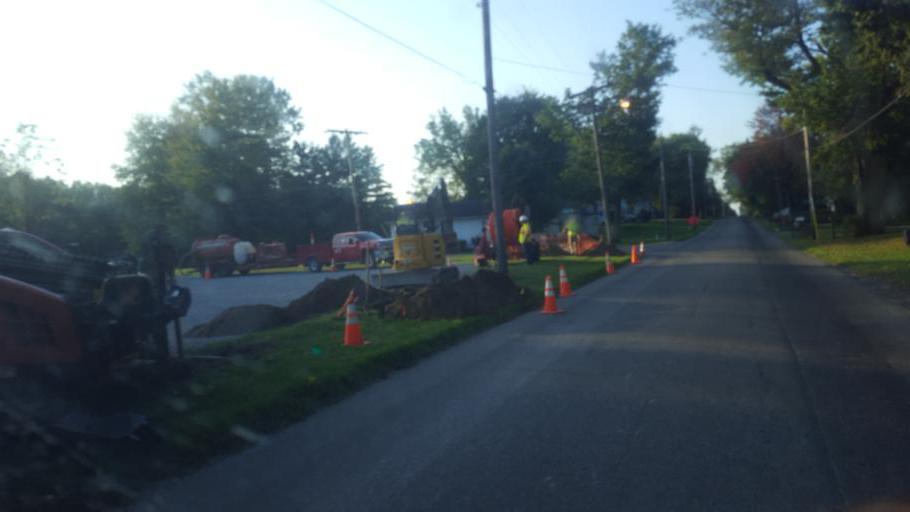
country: US
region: Indiana
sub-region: LaGrange County
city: Lagrange
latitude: 41.6401
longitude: -85.4249
